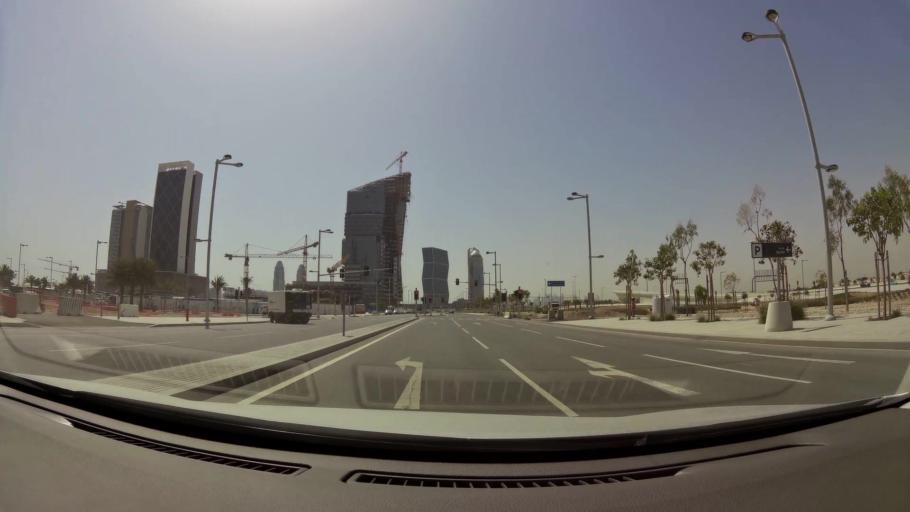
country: QA
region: Baladiyat ad Dawhah
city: Doha
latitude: 25.3863
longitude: 51.5212
